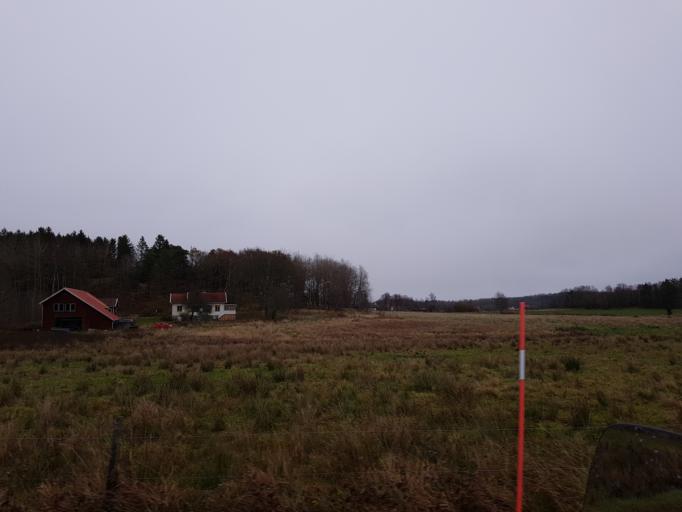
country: SE
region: Vaestra Goetaland
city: Svanesund
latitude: 58.2045
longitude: 11.7758
